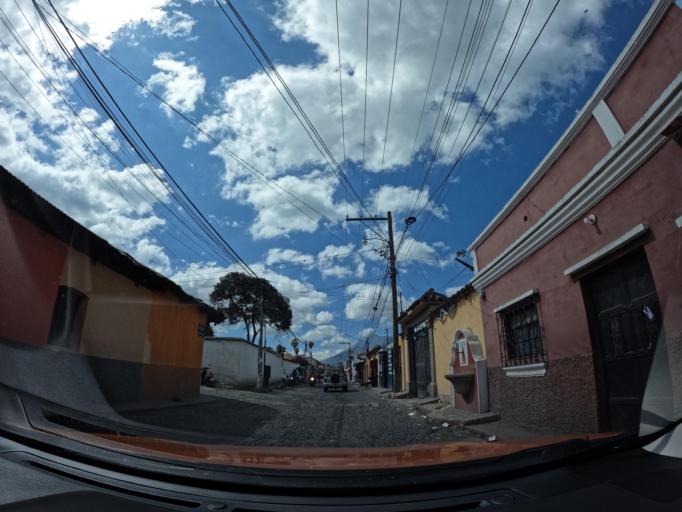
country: GT
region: Sacatepequez
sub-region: Municipio de Santa Maria de Jesus
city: Santa Maria de Jesus
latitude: 14.5319
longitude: -90.7380
